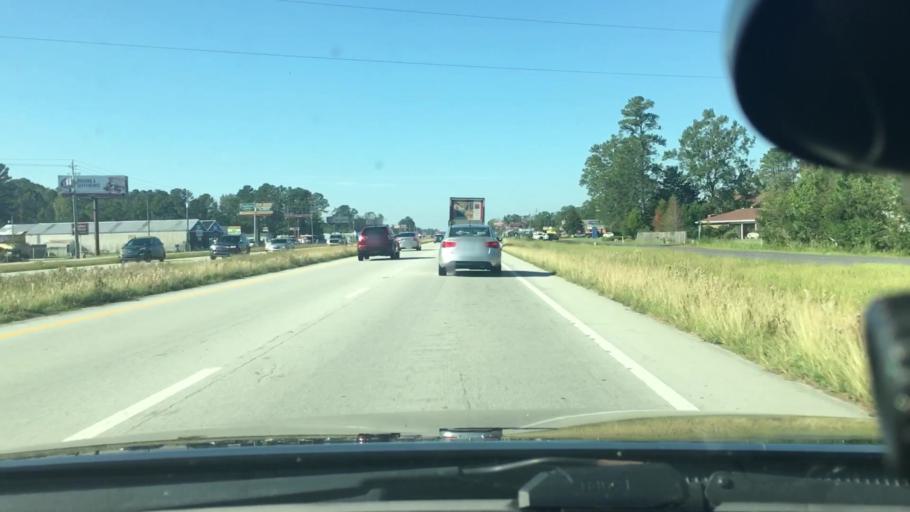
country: US
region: North Carolina
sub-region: Craven County
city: James City
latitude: 35.0590
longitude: -77.0191
